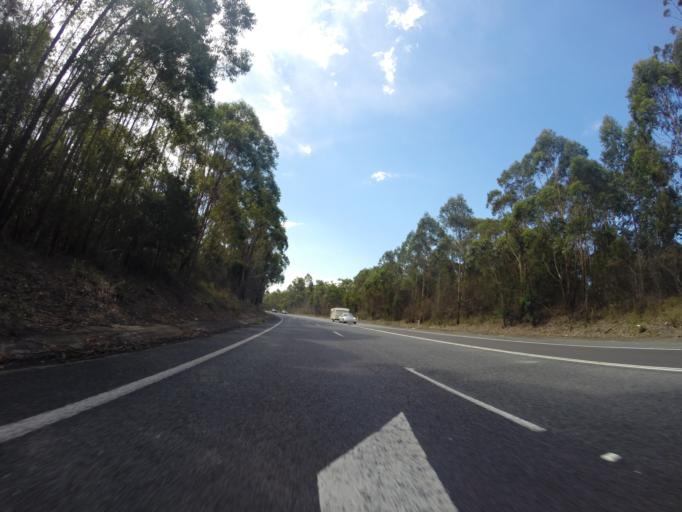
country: AU
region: New South Wales
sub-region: Shoalhaven Shire
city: Falls Creek
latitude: -35.0361
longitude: 150.5840
